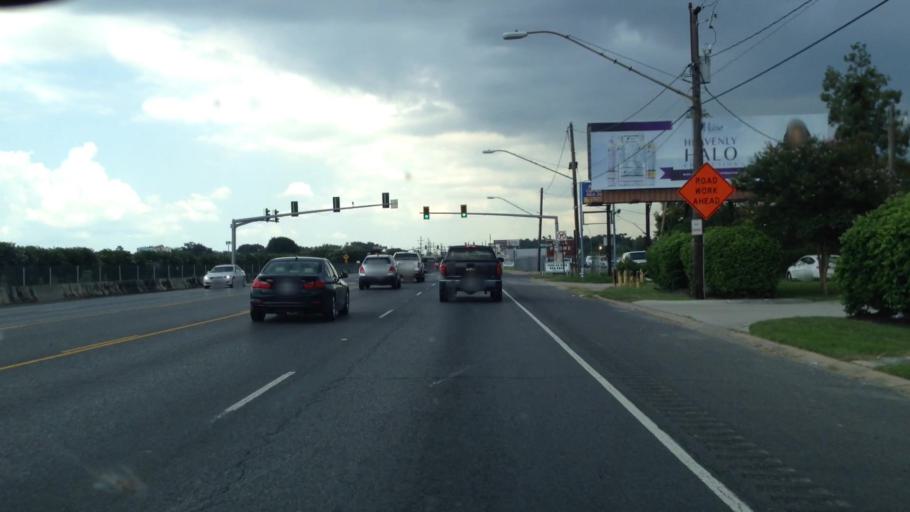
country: US
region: Louisiana
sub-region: Jefferson Parish
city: Kenner
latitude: 29.9817
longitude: -90.2546
